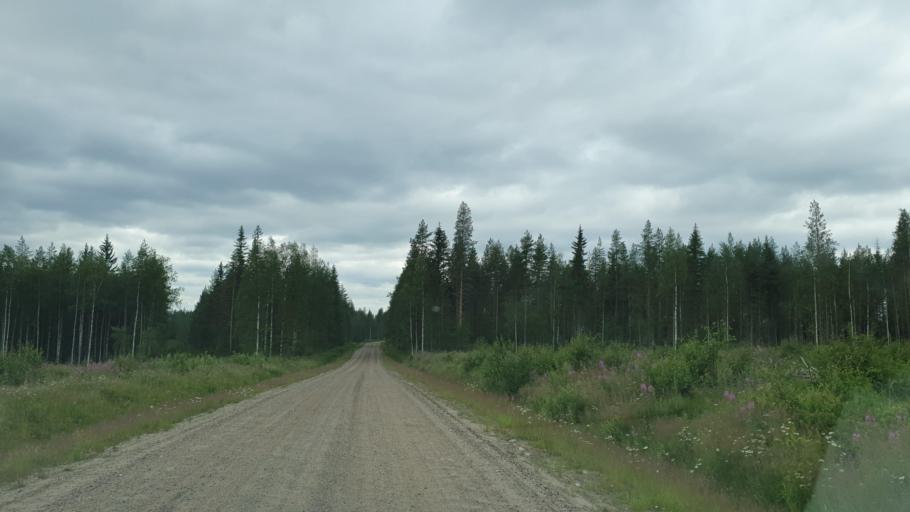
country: FI
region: Kainuu
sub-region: Kehys-Kainuu
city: Kuhmo
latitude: 64.0108
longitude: 29.3470
